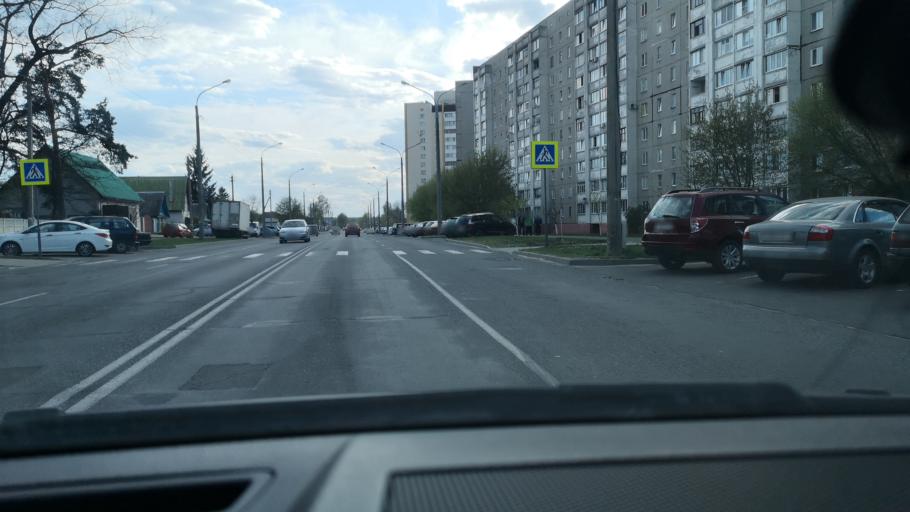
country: BY
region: Gomel
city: Gomel
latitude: 52.4011
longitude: 30.9269
